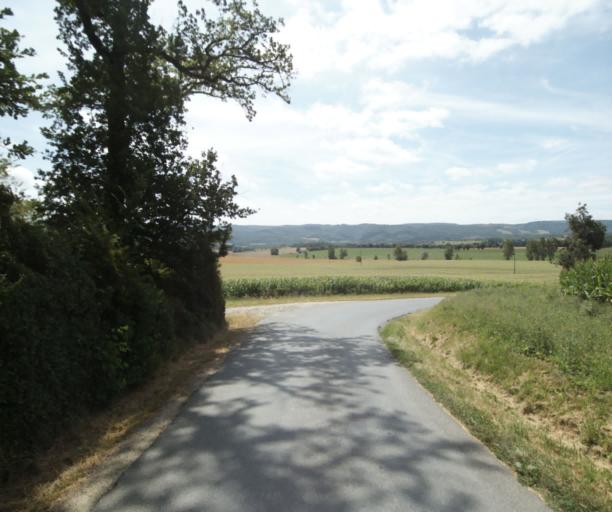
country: FR
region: Midi-Pyrenees
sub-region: Departement du Tarn
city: Dourgne
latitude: 43.5039
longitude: 2.0902
